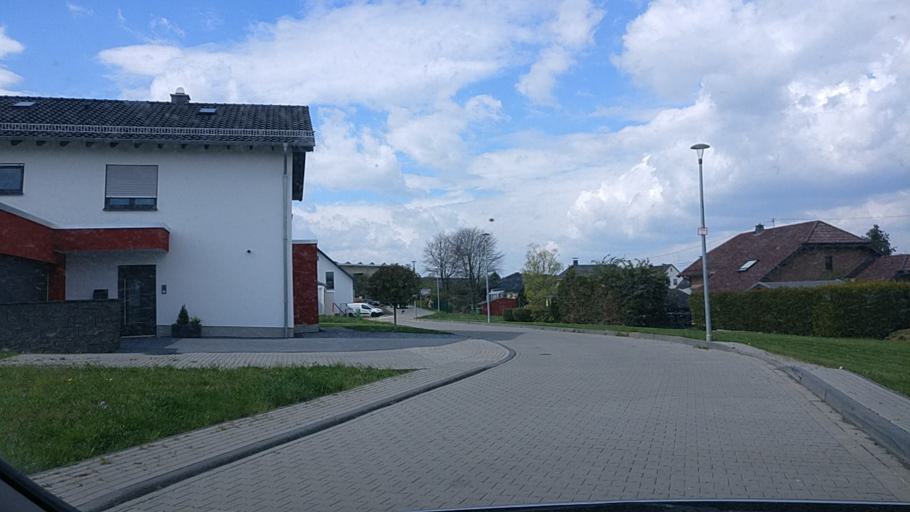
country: DE
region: Rheinland-Pfalz
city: Asbach
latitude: 50.6626
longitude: 7.4274
